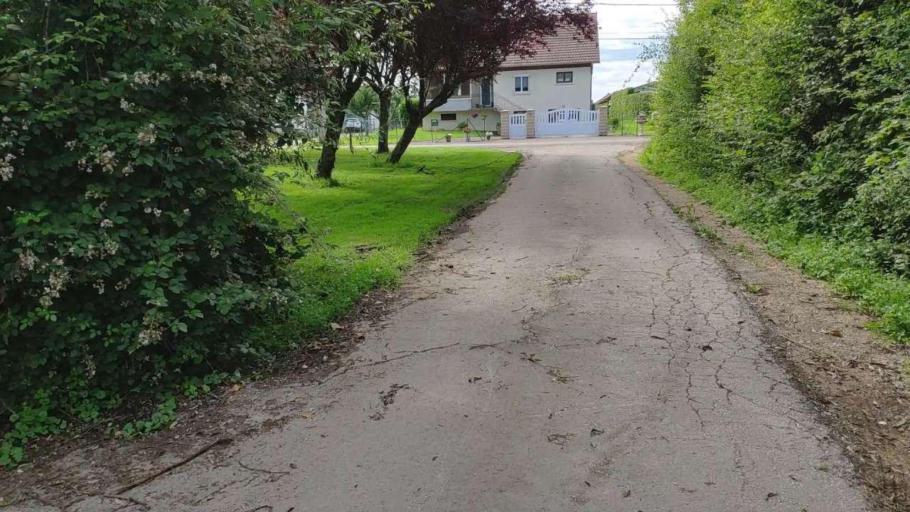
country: FR
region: Franche-Comte
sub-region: Departement du Jura
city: Bletterans
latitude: 46.8031
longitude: 5.4549
